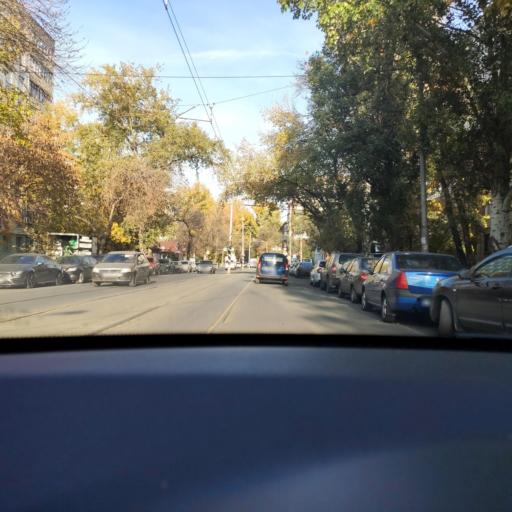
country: RU
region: Samara
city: Samara
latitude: 53.2005
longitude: 50.1369
